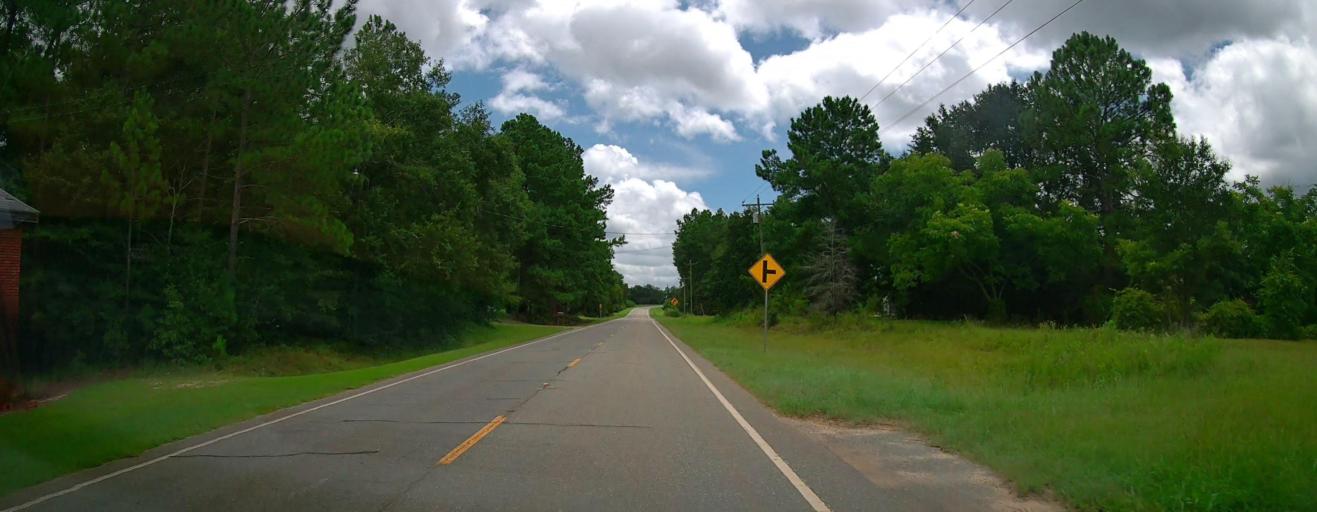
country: US
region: Georgia
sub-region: Wilcox County
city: Rochelle
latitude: 31.9632
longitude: -83.5436
